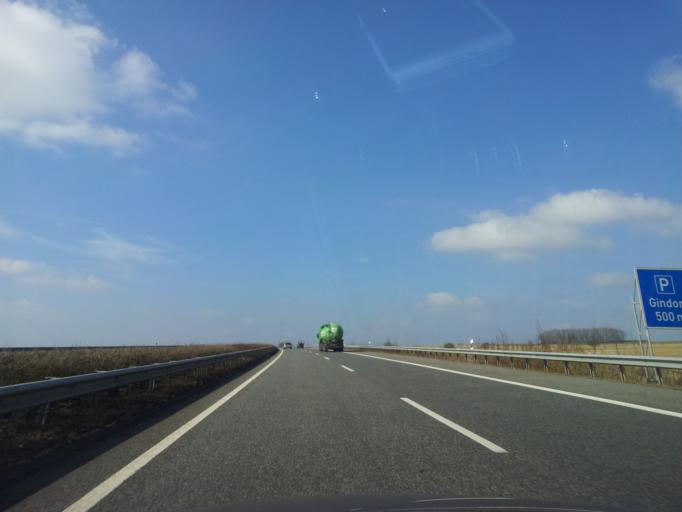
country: DE
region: Rheinland-Pfalz
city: Gindorf
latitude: 50.0212
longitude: 6.6469
